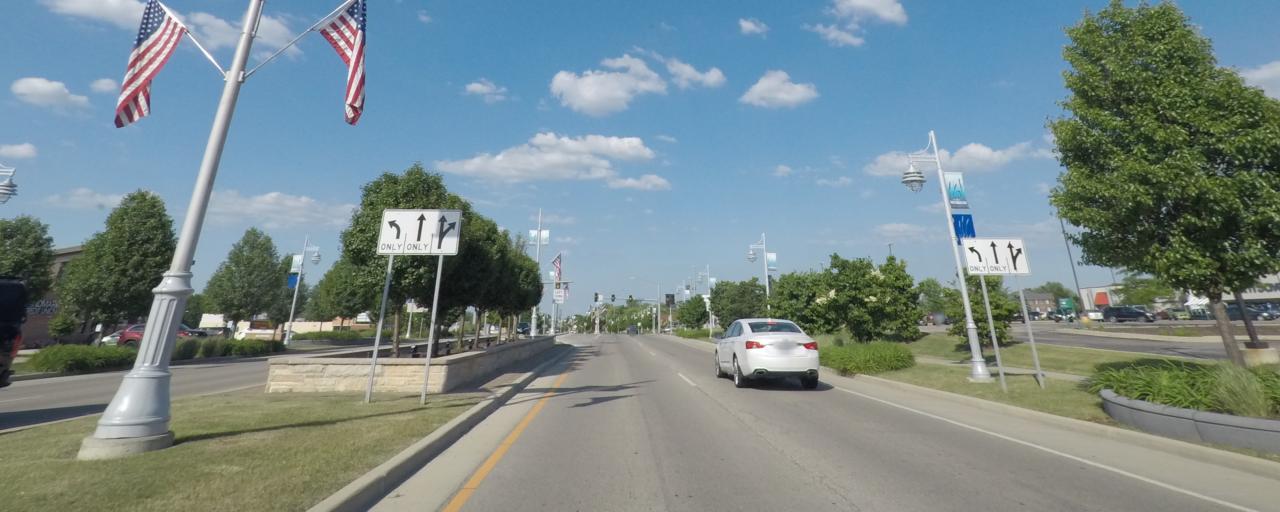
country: US
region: Wisconsin
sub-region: Waukesha County
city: Muskego
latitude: 42.9096
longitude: -88.1261
